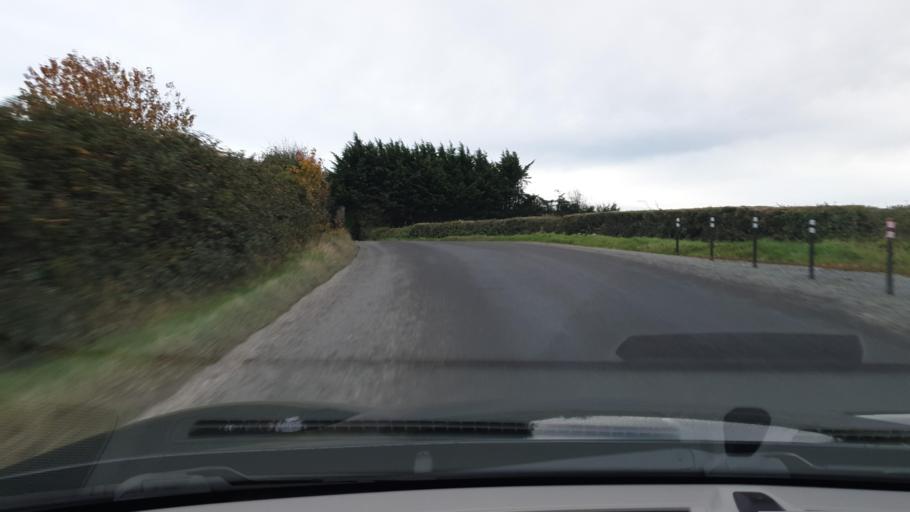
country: IE
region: Leinster
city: Balrothery
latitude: 53.5498
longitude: -6.2274
